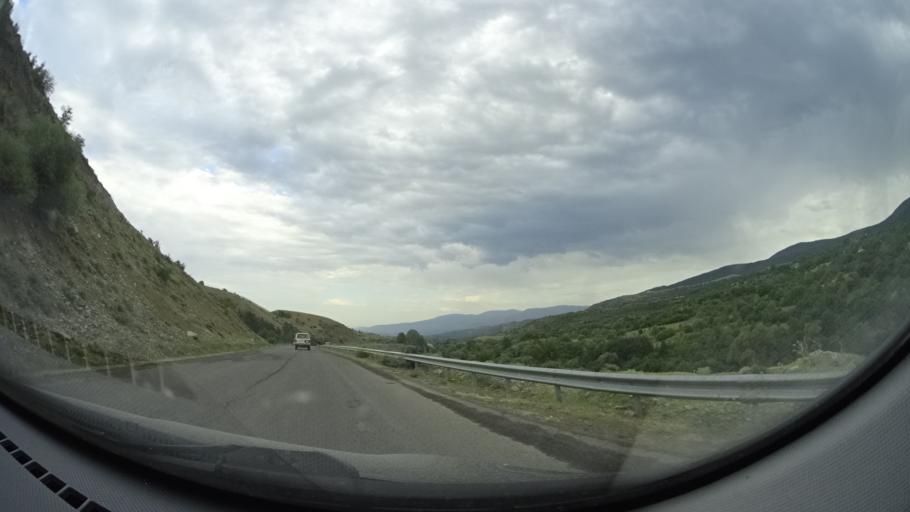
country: GE
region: Samtskhe-Javakheti
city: Adigeni
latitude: 41.6689
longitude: 42.7290
